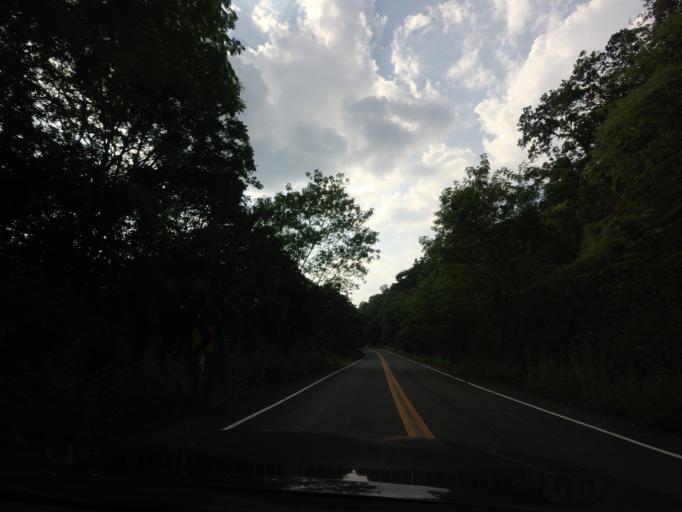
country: TH
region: Nan
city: Na Noi
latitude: 18.2874
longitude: 100.9119
